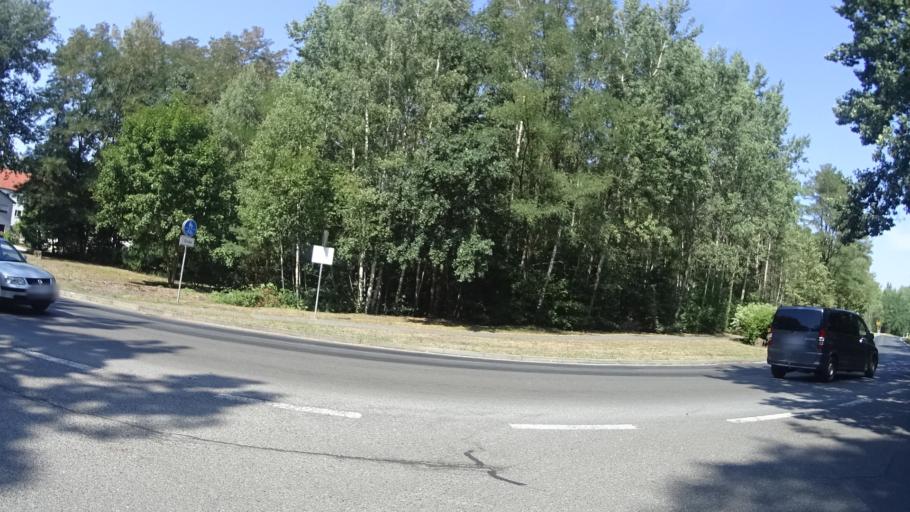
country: DE
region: Saxony
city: Gross Duben
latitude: 51.6030
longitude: 14.5819
